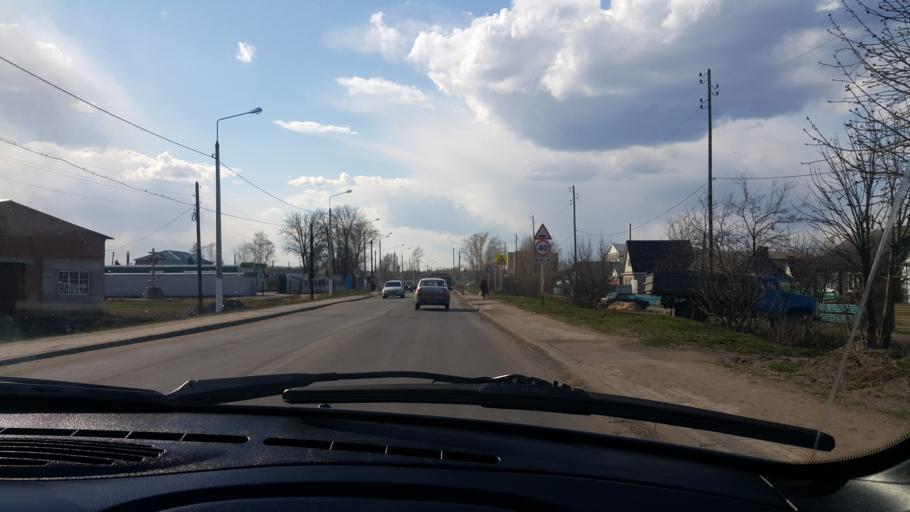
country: RU
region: Tambov
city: Zavoronezhskoye
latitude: 52.8807
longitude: 40.5496
